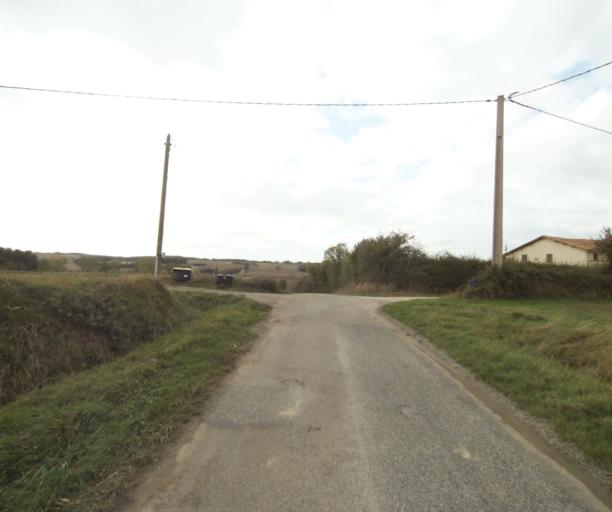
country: FR
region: Midi-Pyrenees
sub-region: Departement du Tarn-et-Garonne
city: Beaumont-de-Lomagne
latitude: 43.8984
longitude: 1.0897
